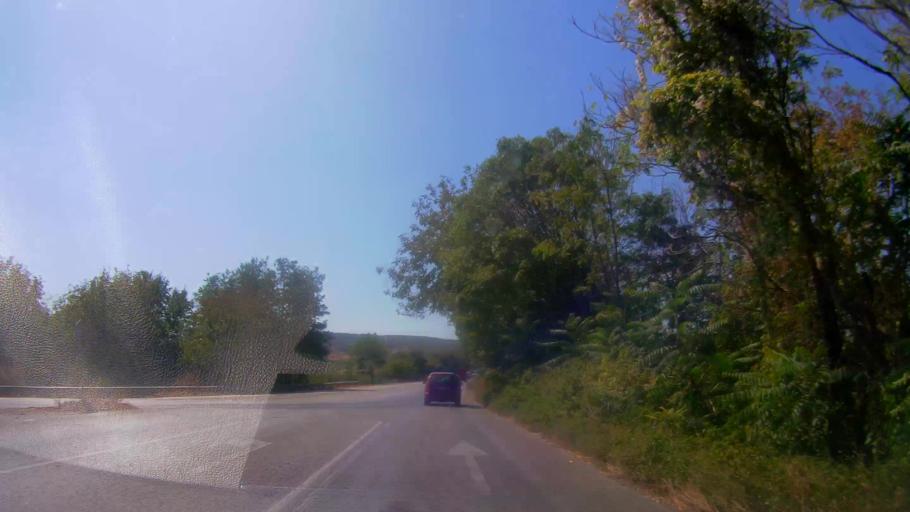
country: BG
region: Veliko Turnovo
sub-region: Obshtina Gorna Oryakhovitsa
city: Purvomaytsi
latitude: 43.1510
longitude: 25.6173
